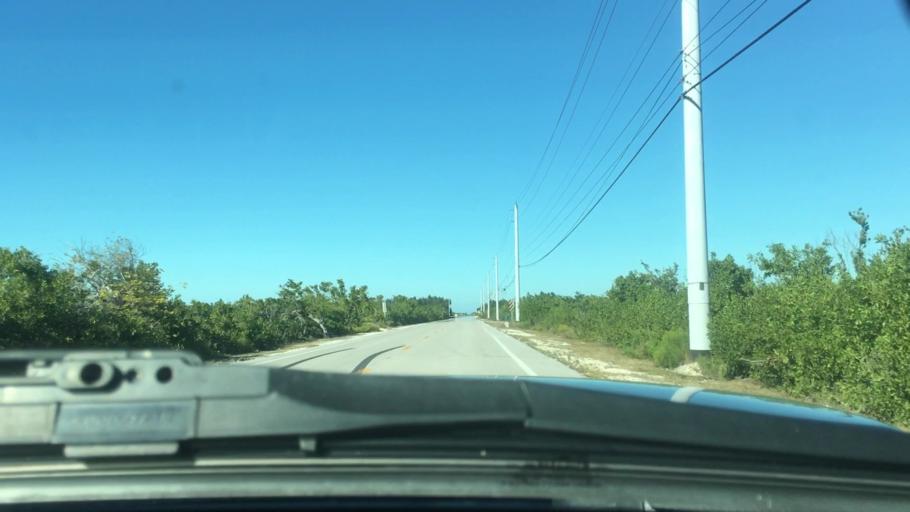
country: US
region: Florida
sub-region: Monroe County
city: Cudjoe Key
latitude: 24.6737
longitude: -81.4996
